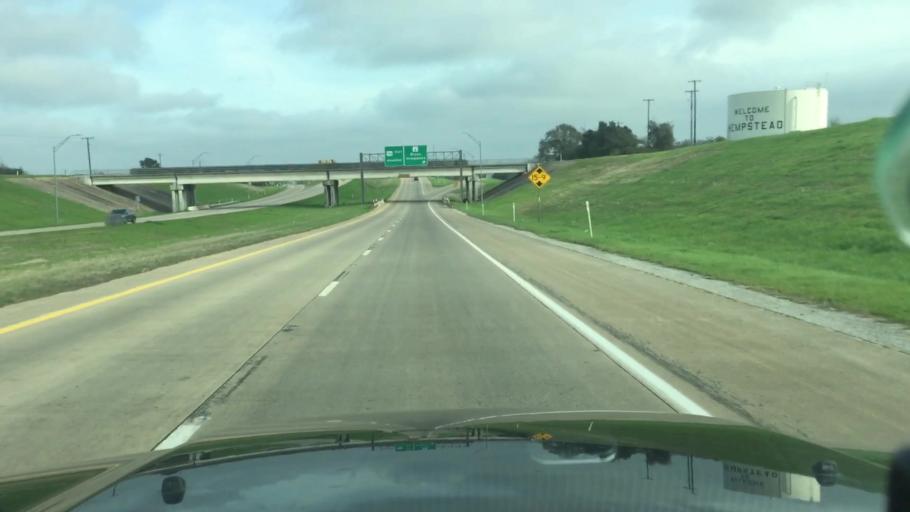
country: US
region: Texas
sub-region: Waller County
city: Hempstead
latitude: 30.1157
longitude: -96.0823
